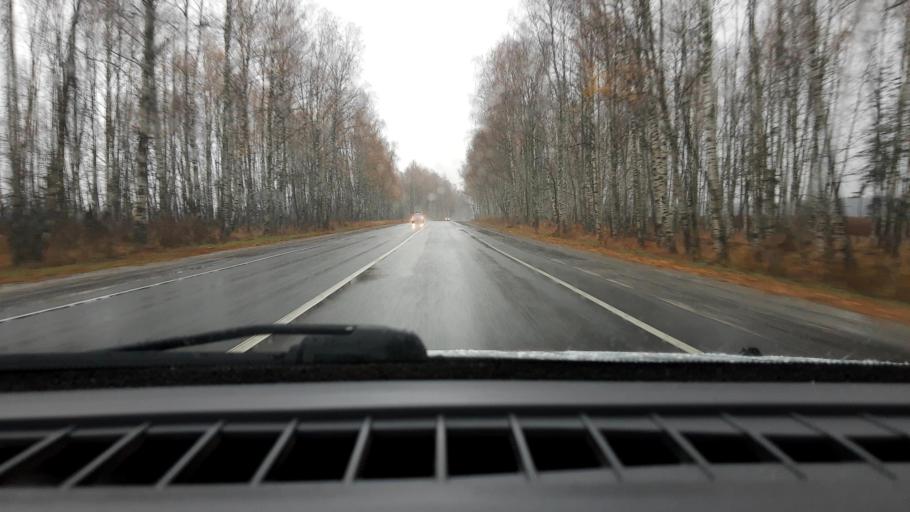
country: RU
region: Nizjnij Novgorod
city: Linda
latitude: 56.6737
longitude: 44.1434
